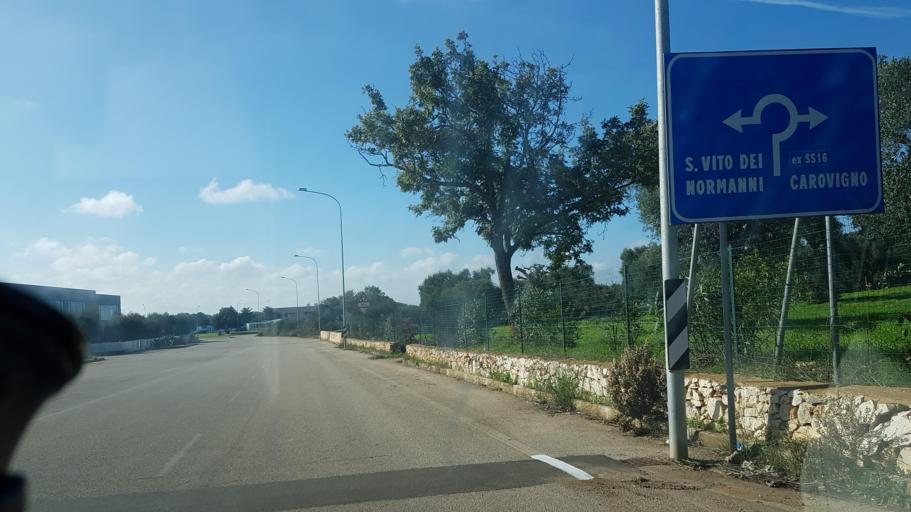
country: IT
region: Apulia
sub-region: Provincia di Brindisi
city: San Vito dei Normanni
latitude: 40.6708
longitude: 17.6973
